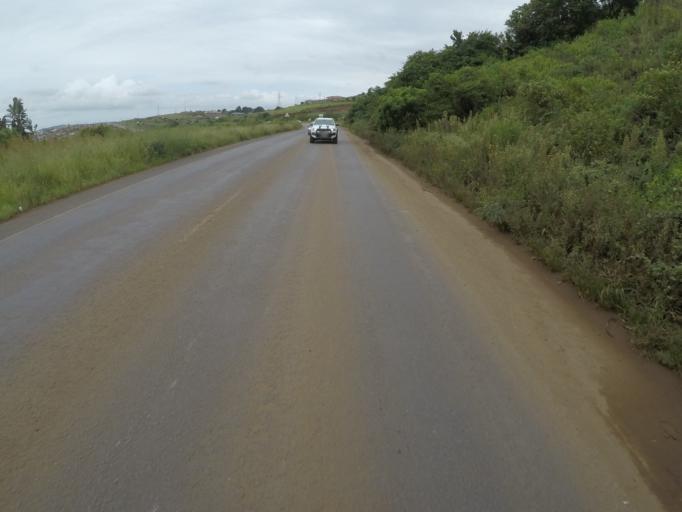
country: ZA
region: KwaZulu-Natal
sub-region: uThungulu District Municipality
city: Empangeni
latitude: -28.7542
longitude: 31.8754
